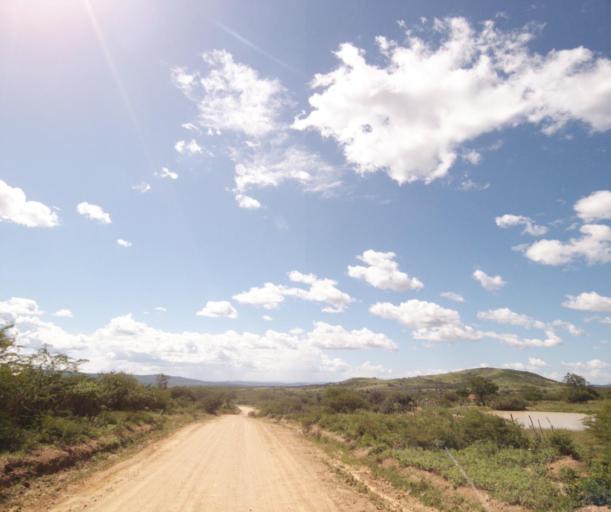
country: BR
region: Bahia
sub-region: Pocoes
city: Pocoes
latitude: -14.2563
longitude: -40.7223
